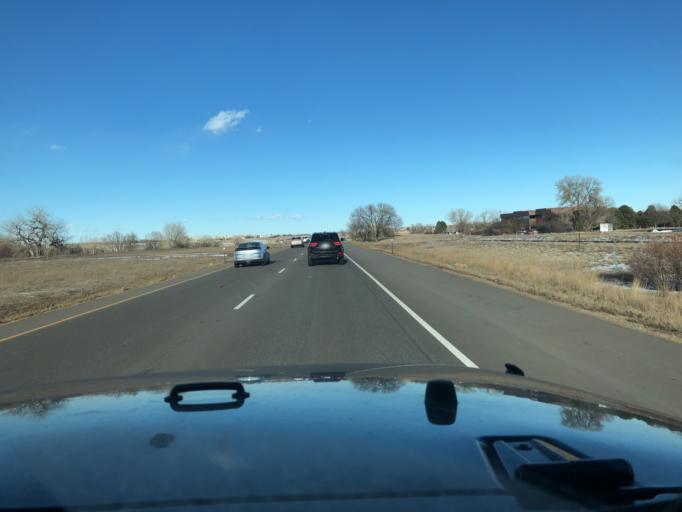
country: US
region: Colorado
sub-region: Boulder County
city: Gunbarrel
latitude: 40.0647
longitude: -105.2170
